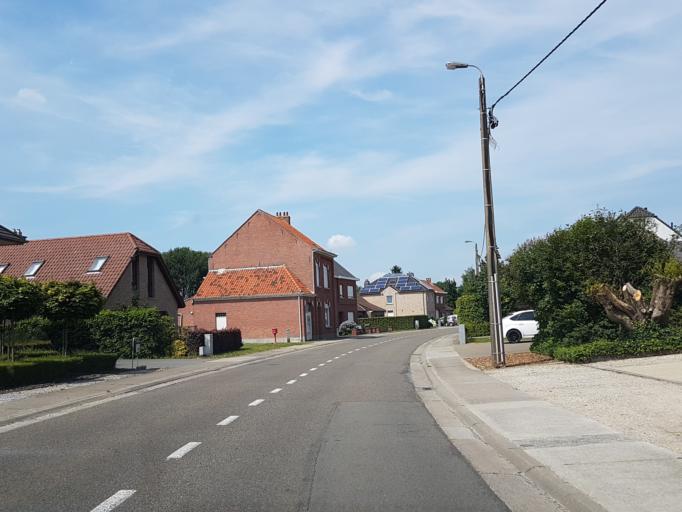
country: BE
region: Flanders
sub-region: Provincie Vlaams-Brabant
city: Kampenhout
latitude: 50.9373
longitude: 4.5639
